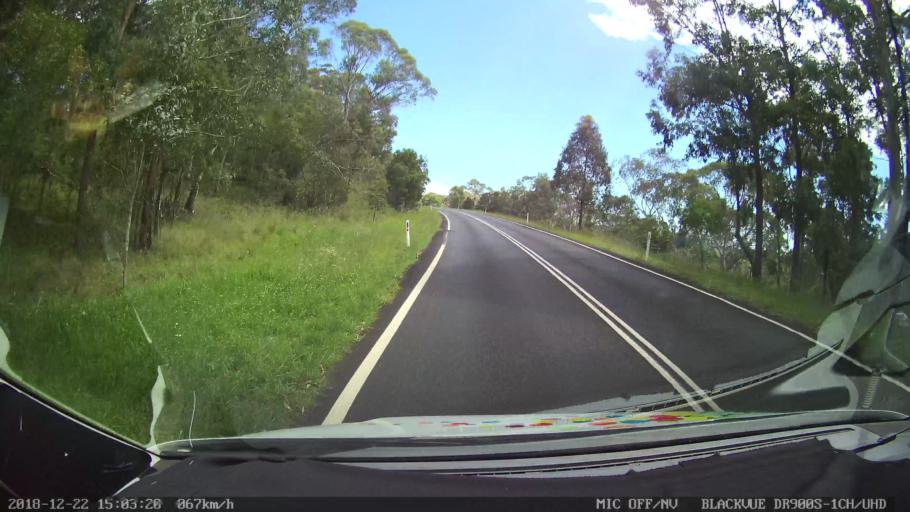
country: AU
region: New South Wales
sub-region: Bellingen
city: Dorrigo
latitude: -30.2635
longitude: 152.4415
